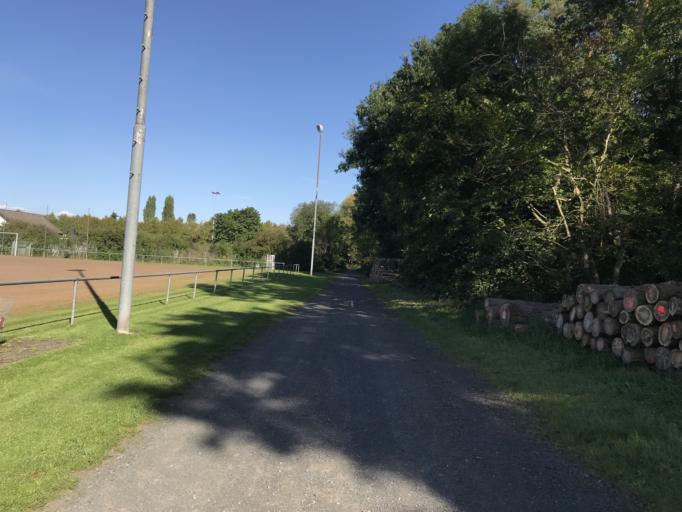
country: DE
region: Hesse
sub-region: Regierungsbezirk Darmstadt
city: Altenstadt
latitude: 50.2740
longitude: 8.9534
